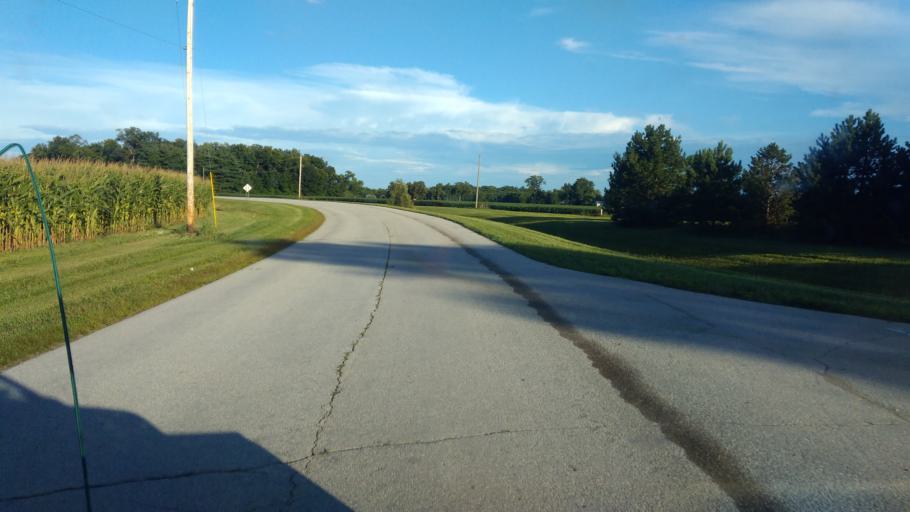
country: US
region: Ohio
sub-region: Wyandot County
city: Upper Sandusky
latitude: 40.8624
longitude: -83.2652
